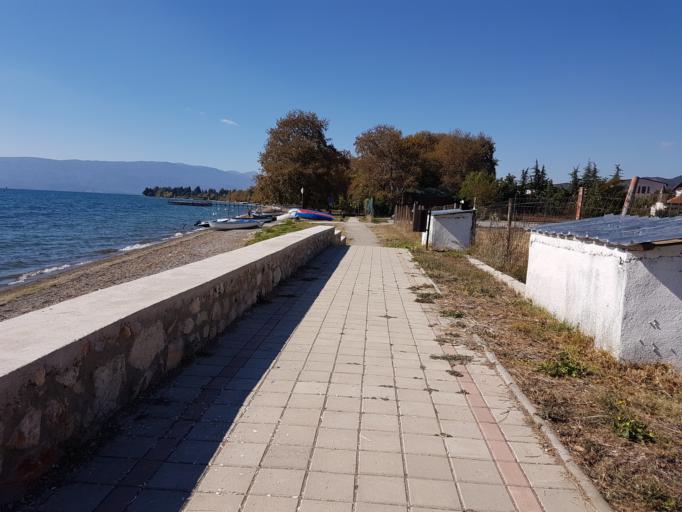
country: MK
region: Ohrid
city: Ohrid
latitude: 41.1179
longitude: 20.7868
